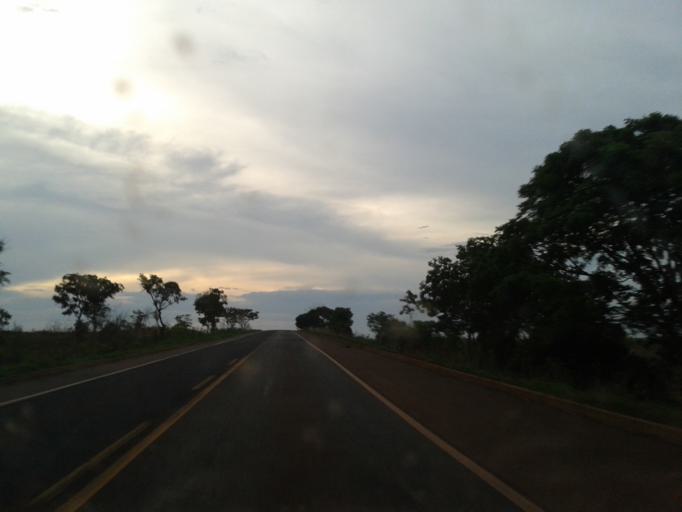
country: BR
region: Goias
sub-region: Santa Helena De Goias
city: Santa Helena de Goias
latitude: -17.8953
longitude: -50.6538
